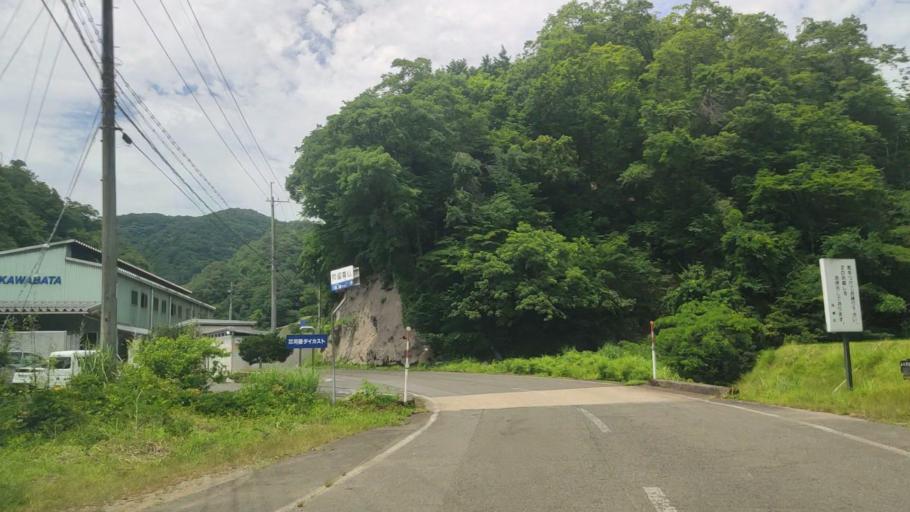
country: JP
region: Hyogo
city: Toyooka
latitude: 35.5232
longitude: 134.6985
